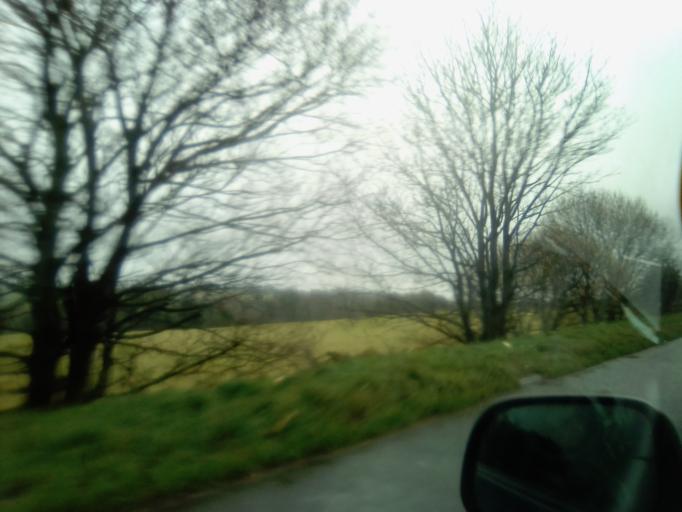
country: GB
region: Northern Ireland
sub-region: Strabane District
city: Sion Mills
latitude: 54.7486
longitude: -7.4449
